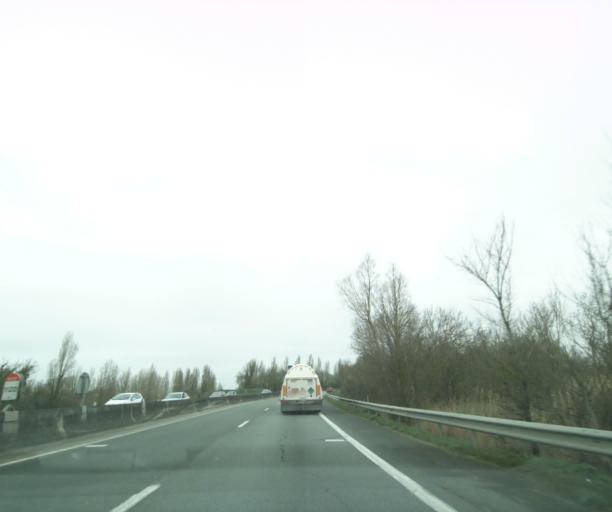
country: FR
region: Poitou-Charentes
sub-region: Departement de la Charente-Maritime
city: Angoulins
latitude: 46.1208
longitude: -1.1093
